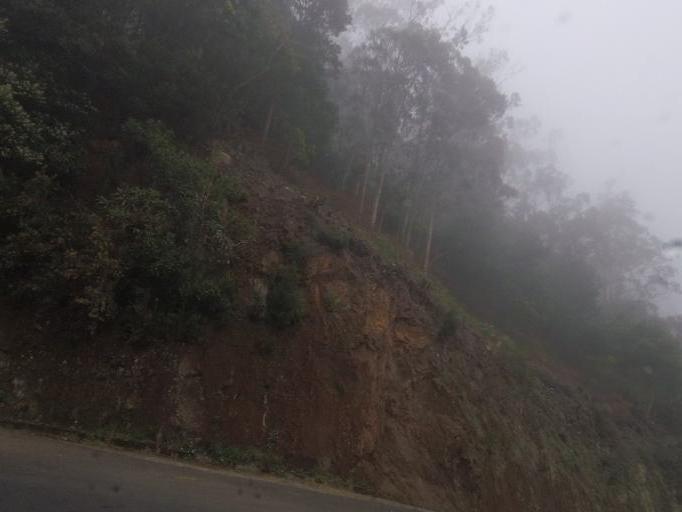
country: PT
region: Madeira
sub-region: Santa Cruz
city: Santa Cruz
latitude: 32.7279
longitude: -16.8213
